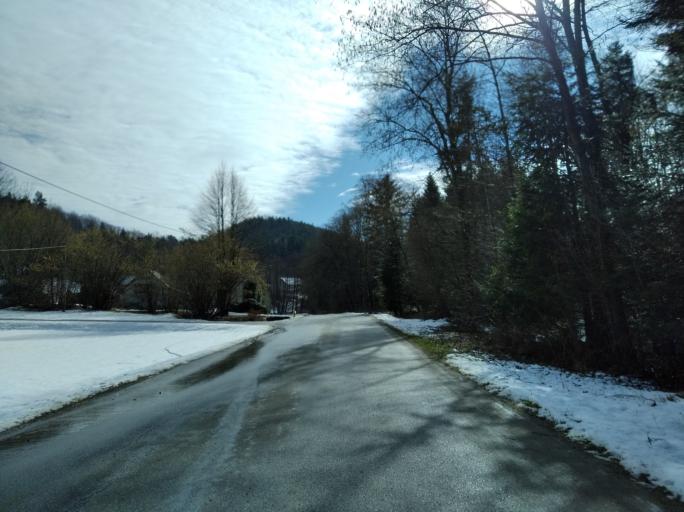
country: PL
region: Subcarpathian Voivodeship
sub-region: Powiat brzozowski
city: Jablonica Polska
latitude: 49.7443
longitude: 21.8839
